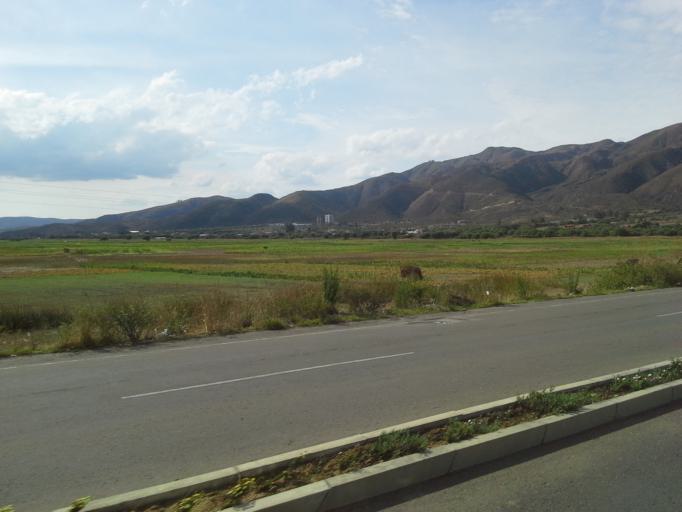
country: BO
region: Cochabamba
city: Tarata
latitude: -17.5528
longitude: -66.0072
